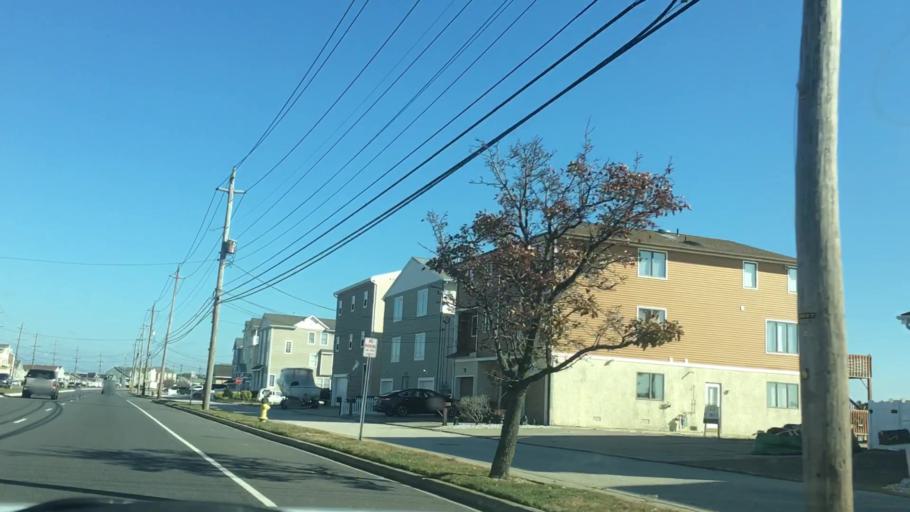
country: US
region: New Jersey
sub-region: Atlantic County
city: Atlantic City
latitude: 39.3923
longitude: -74.4075
